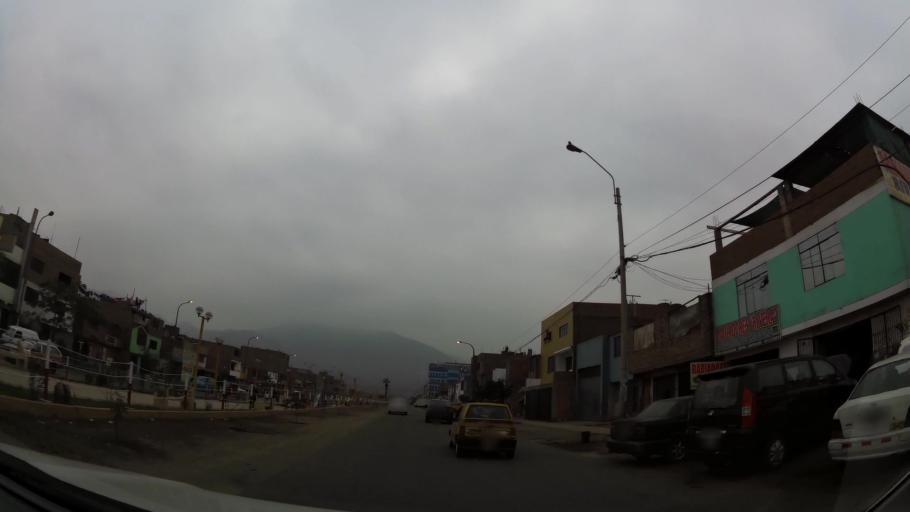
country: PE
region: Lima
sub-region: Lima
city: Independencia
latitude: -11.9681
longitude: -76.9952
